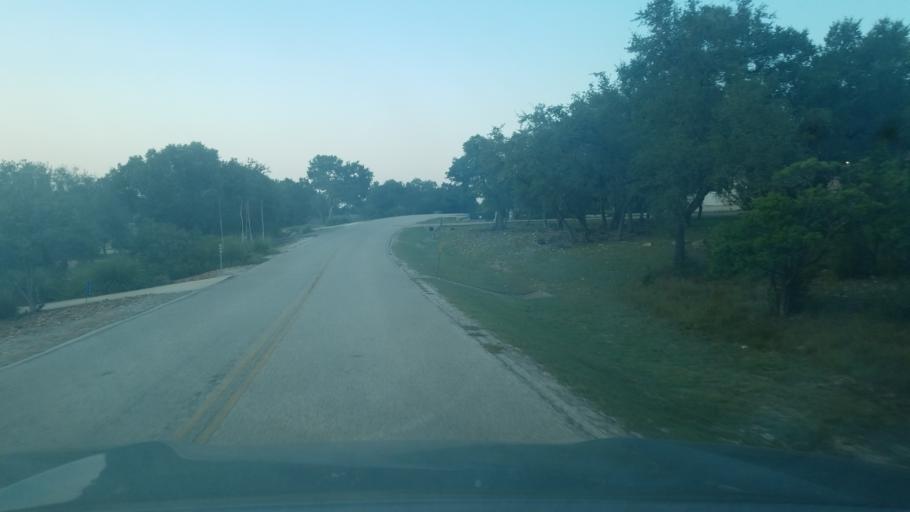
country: US
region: Texas
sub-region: Comal County
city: Bulverde
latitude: 29.8277
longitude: -98.4028
